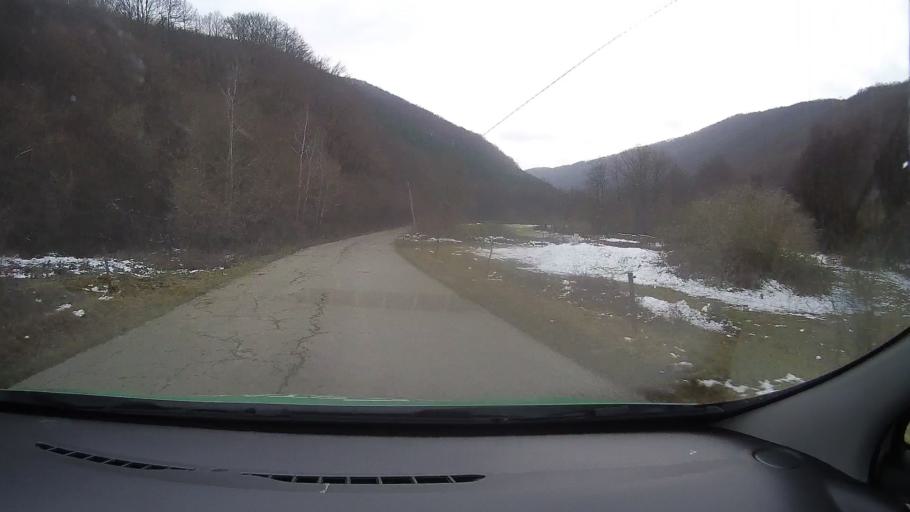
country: RO
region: Hunedoara
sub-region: Comuna Balsa
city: Balsa
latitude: 46.0106
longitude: 23.1507
